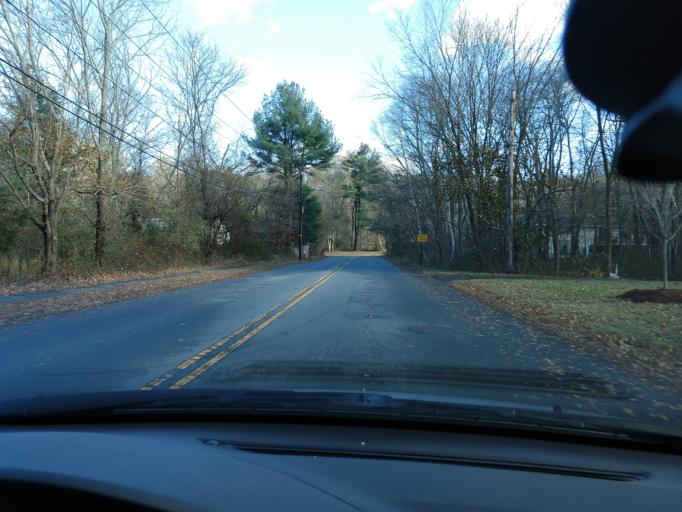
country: US
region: Massachusetts
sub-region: Middlesex County
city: Bedford
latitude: 42.5135
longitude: -71.2633
